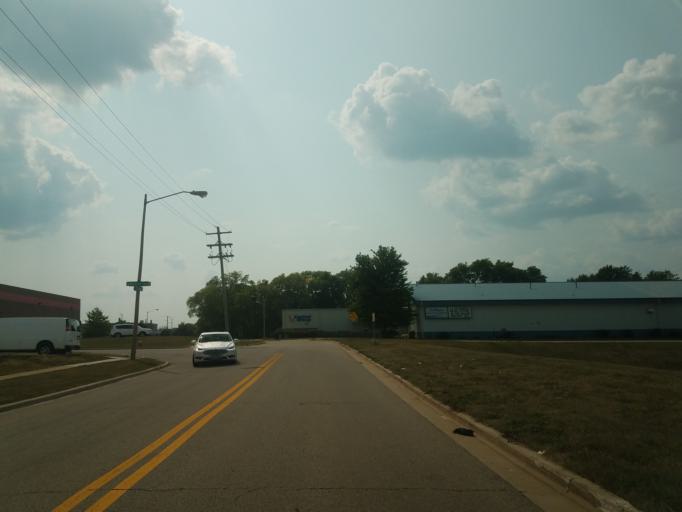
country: US
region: Illinois
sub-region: McLean County
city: Bloomington
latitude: 40.4609
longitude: -88.9752
